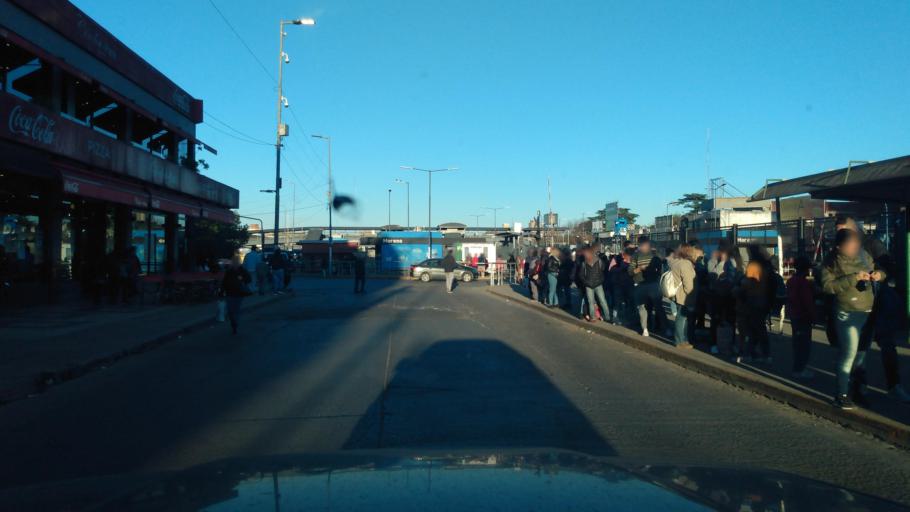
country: AR
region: Buenos Aires
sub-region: Partido de Merlo
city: Merlo
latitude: -34.6497
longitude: -58.7921
